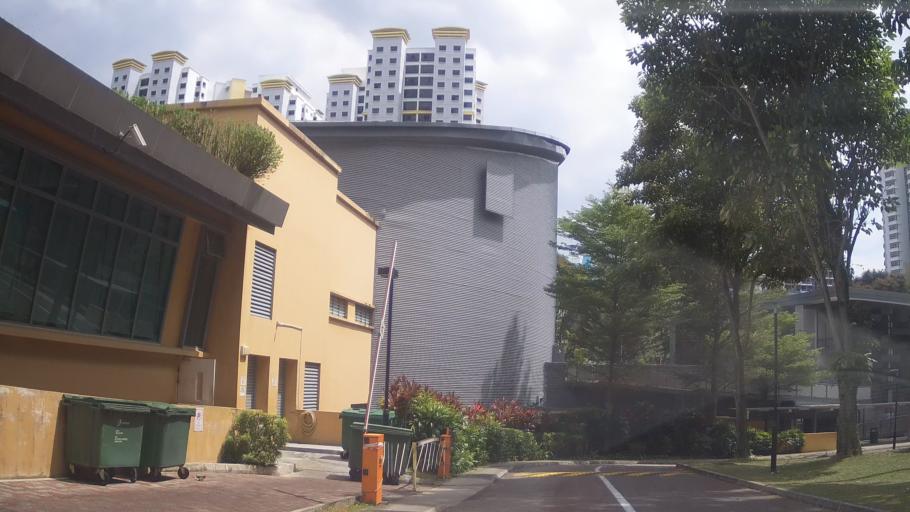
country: MY
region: Johor
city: Johor Bahru
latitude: 1.3820
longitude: 103.7645
